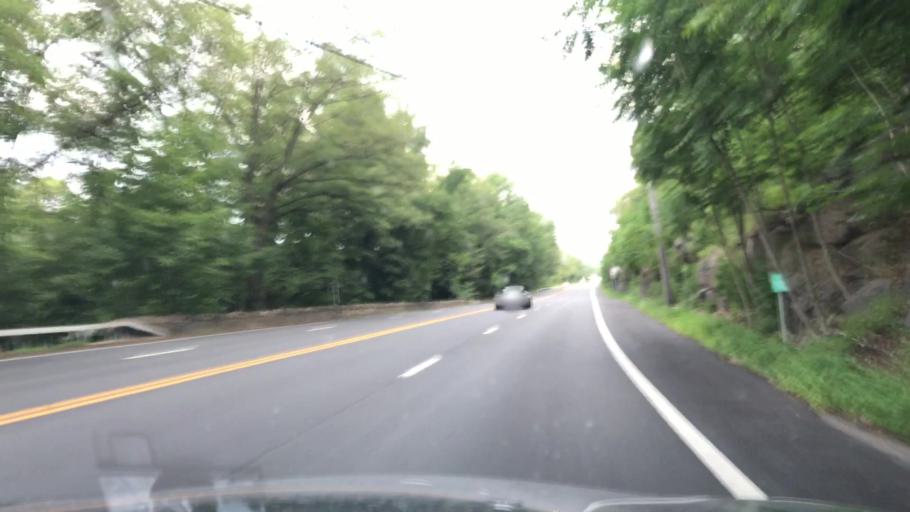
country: US
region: New York
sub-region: Rockland County
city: Sloatsburg
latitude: 41.1843
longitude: -74.1836
